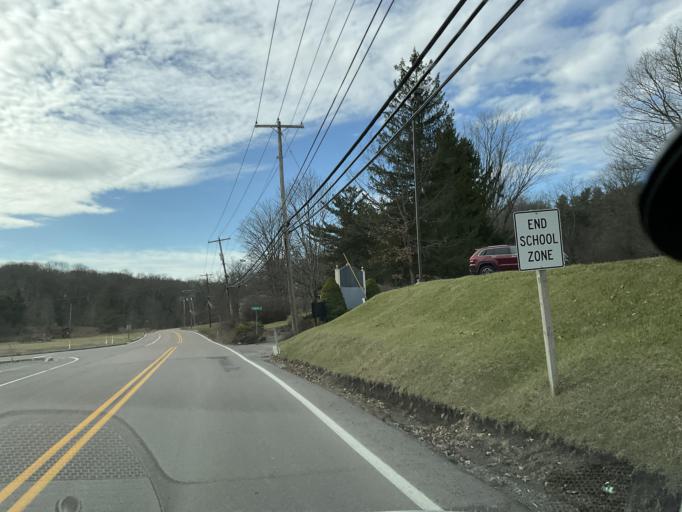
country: US
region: Maryland
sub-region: Garrett County
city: Mountain Lake Park
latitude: 39.4031
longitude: -79.3918
